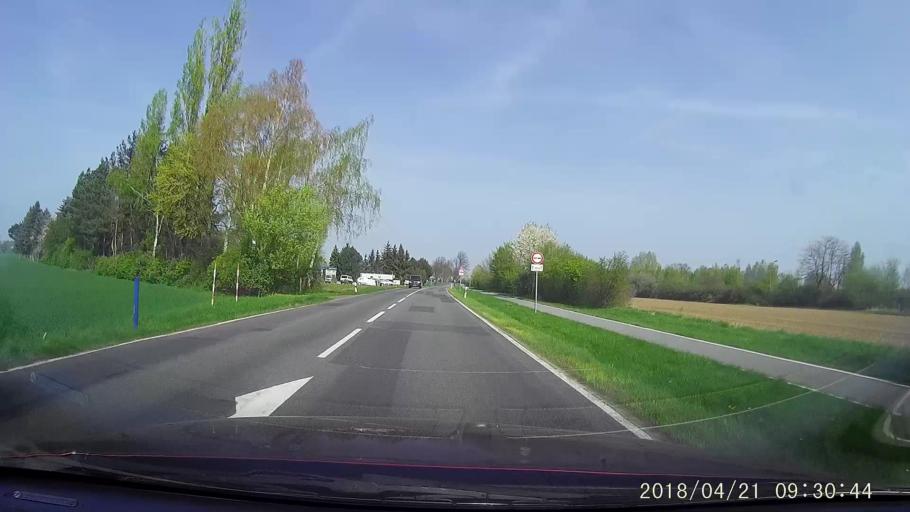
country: DE
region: Saxony
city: Bautzen
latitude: 51.2037
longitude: 14.4033
